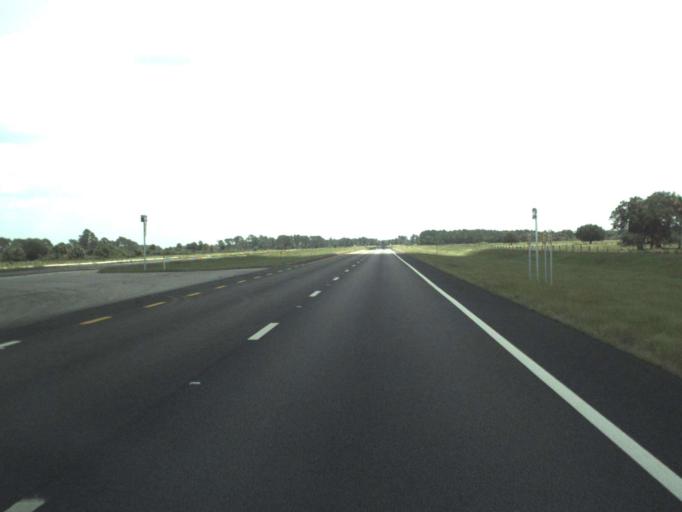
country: US
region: Florida
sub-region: Okeechobee County
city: Cypress Quarters
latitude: 27.3490
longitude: -80.6366
